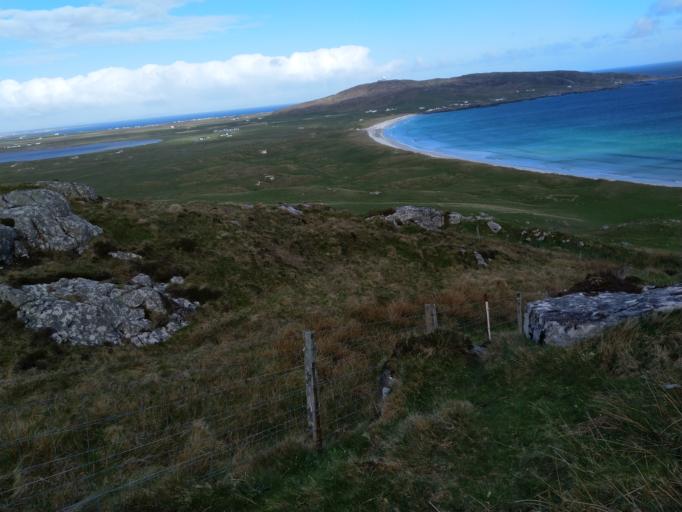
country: GB
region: Scotland
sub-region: Eilean Siar
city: Barra
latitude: 56.4612
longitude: -6.9715
